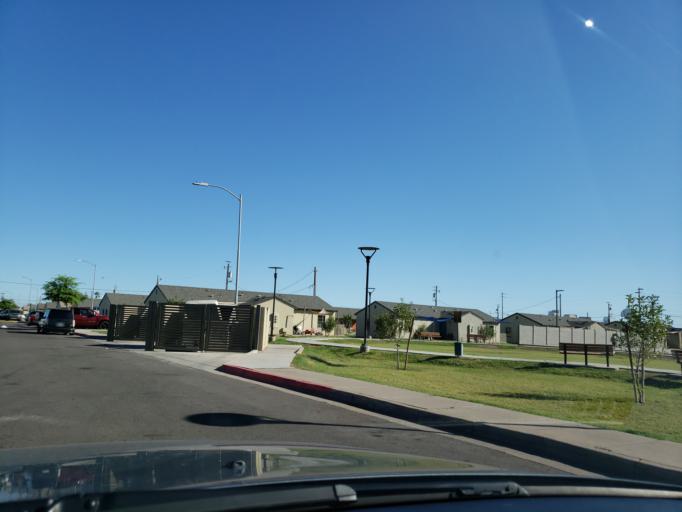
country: US
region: Arizona
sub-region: Maricopa County
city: Phoenix
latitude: 33.4335
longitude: -112.1022
